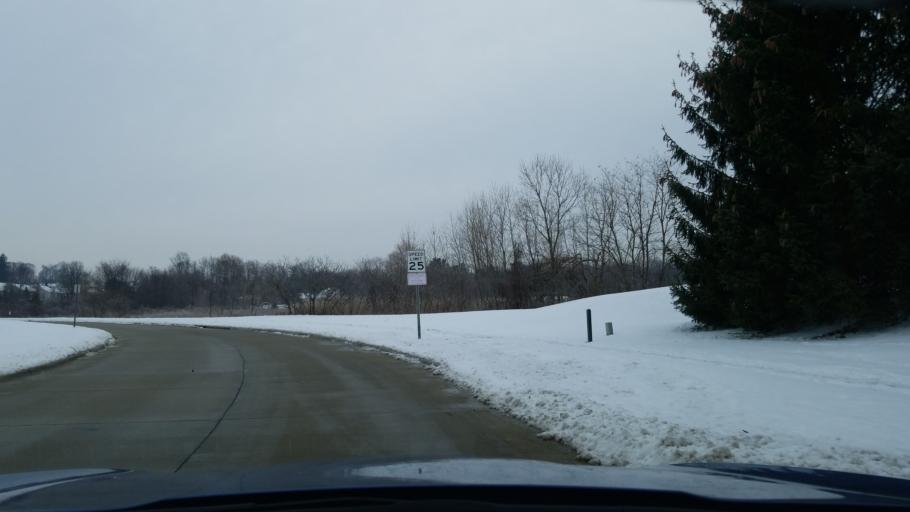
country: US
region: Ohio
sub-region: Summit County
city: Northfield
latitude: 41.3309
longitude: -81.5479
